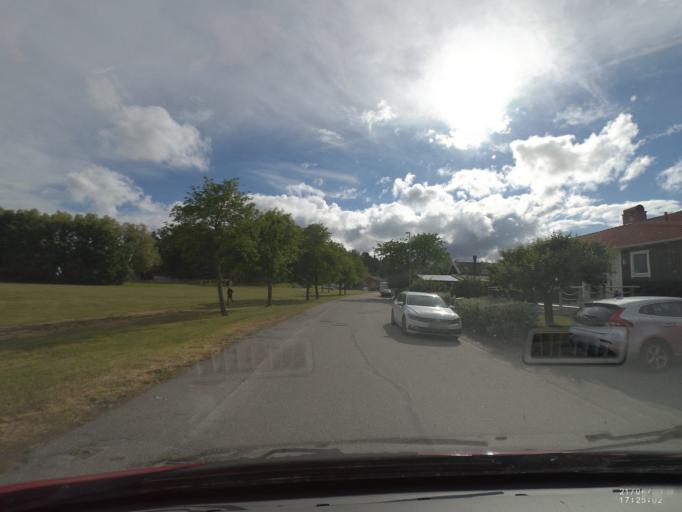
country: SE
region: Soedermanland
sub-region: Nykopings Kommun
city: Nykoping
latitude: 58.7513
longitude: 17.0535
